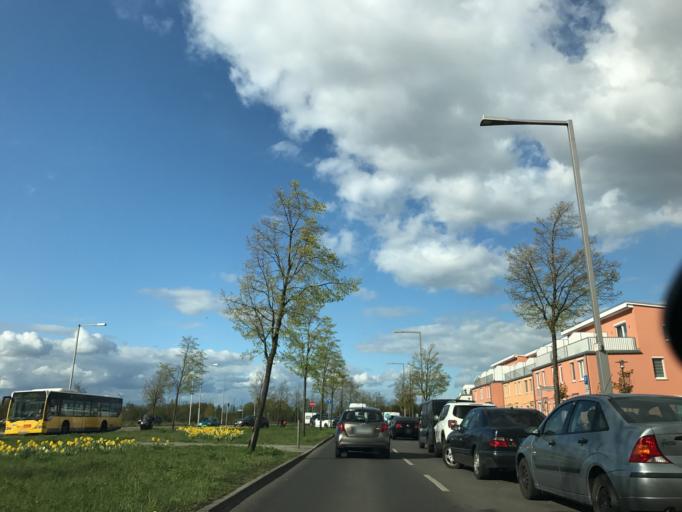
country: DE
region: Berlin
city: Haselhorst
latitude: 52.5561
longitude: 13.2263
